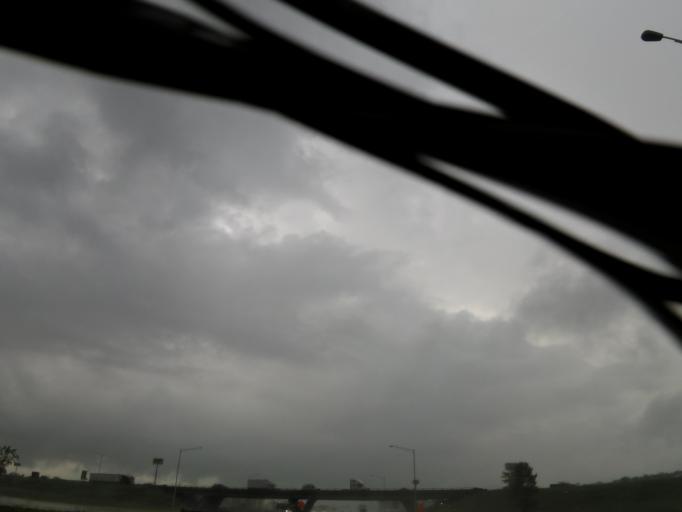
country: US
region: Illinois
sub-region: Jefferson County
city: Mount Vernon
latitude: 38.3114
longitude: -88.9514
